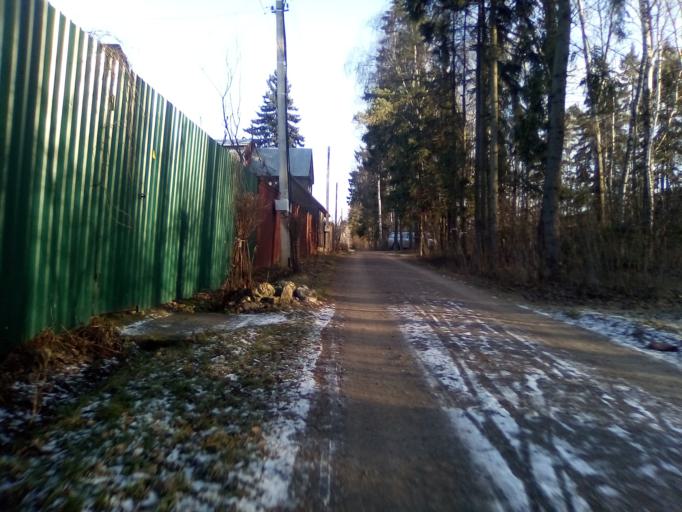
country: RU
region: Moskovskaya
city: Lesnoy Gorodok
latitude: 55.6648
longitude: 37.2004
